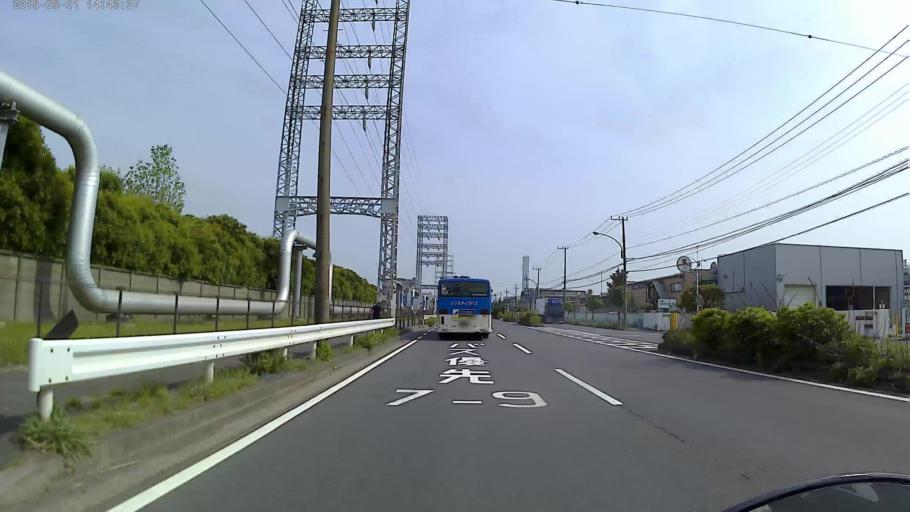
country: JP
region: Kanagawa
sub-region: Kawasaki-shi
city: Kawasaki
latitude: 35.5198
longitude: 139.7564
